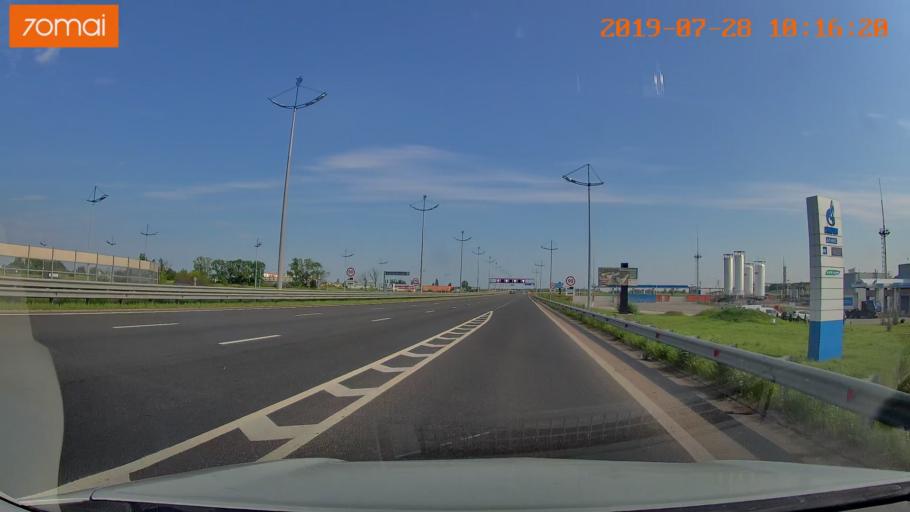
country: RU
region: Kaliningrad
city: Bol'shoe Isakovo
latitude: 54.7261
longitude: 20.5976
